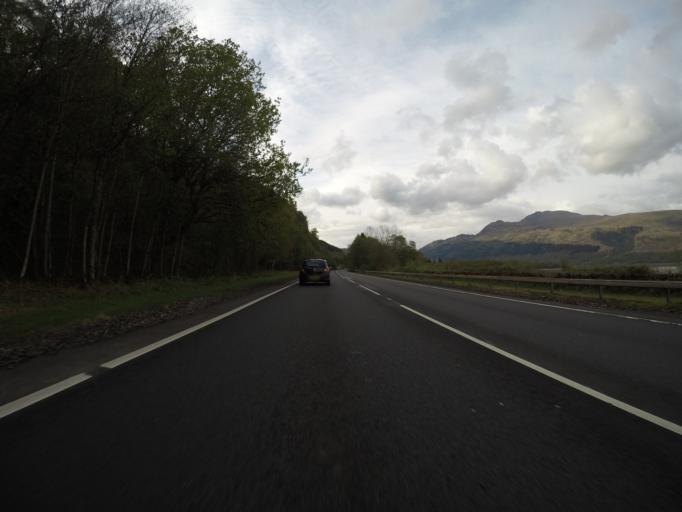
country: GB
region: Scotland
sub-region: Argyll and Bute
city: Helensburgh
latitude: 56.1413
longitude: -4.6621
